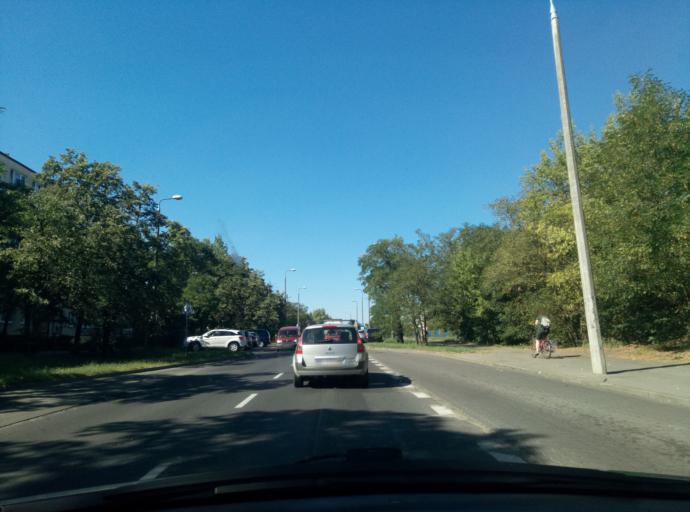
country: PL
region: Kujawsko-Pomorskie
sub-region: Torun
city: Torun
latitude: 53.0296
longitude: 18.6014
